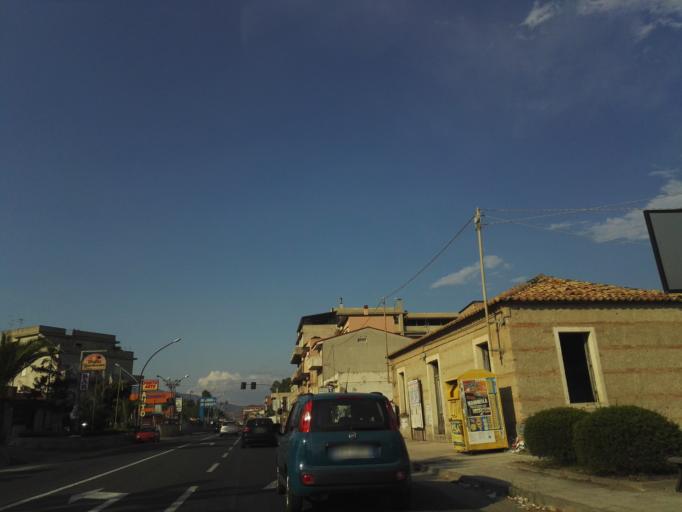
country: IT
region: Calabria
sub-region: Provincia di Reggio Calabria
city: Siderno
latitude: 38.2797
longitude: 16.3097
